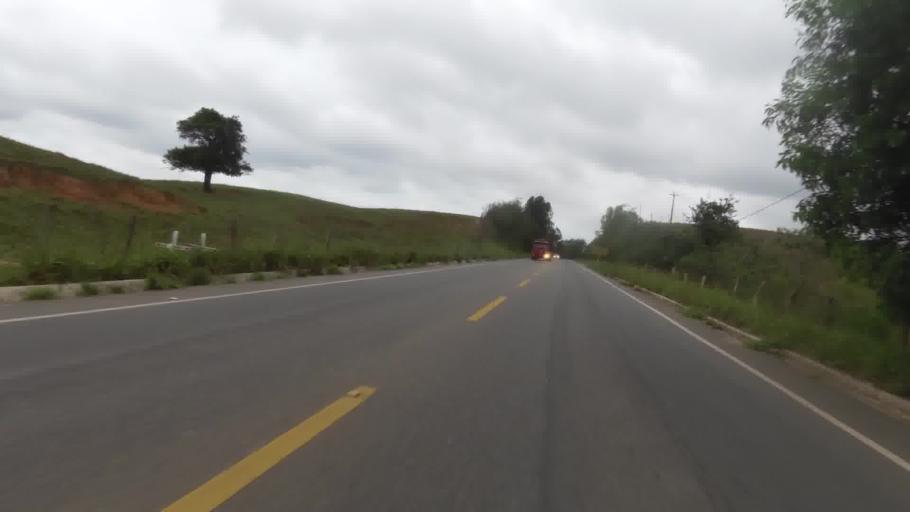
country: BR
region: Espirito Santo
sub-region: Iconha
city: Iconha
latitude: -20.7798
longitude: -40.7571
